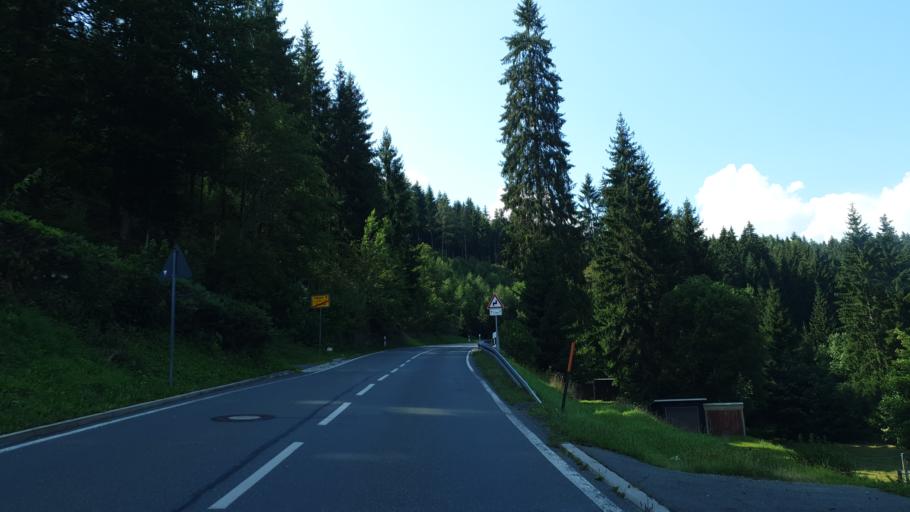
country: DE
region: Saxony
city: Zwota
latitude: 50.3565
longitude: 12.4229
